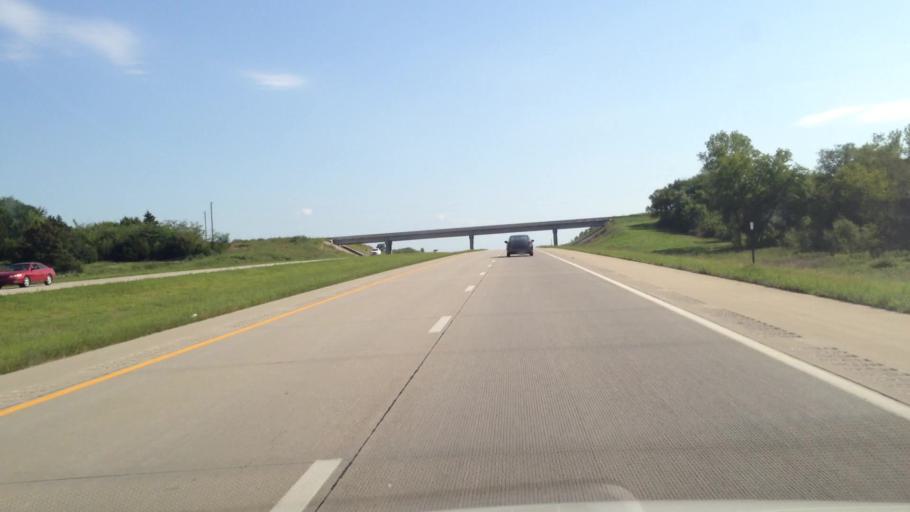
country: US
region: Kansas
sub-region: Linn County
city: Pleasanton
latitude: 38.1128
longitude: -94.7137
